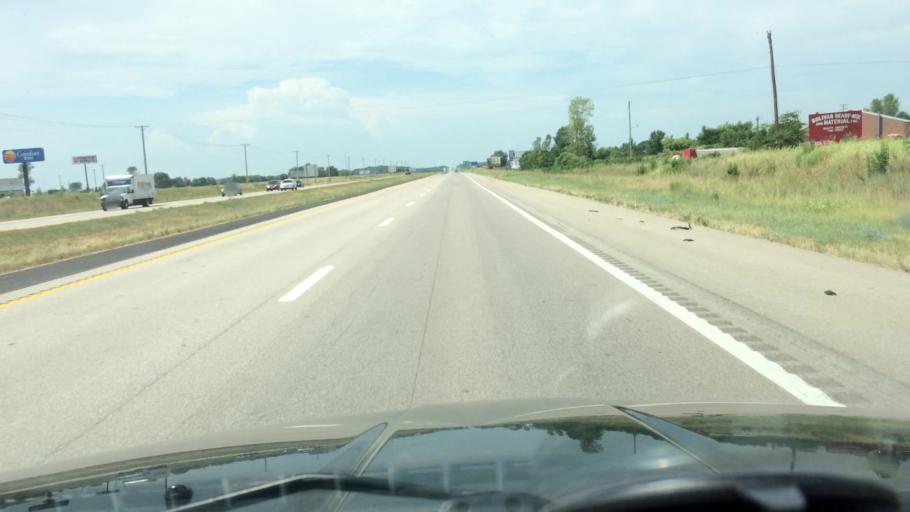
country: US
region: Missouri
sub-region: Polk County
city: Bolivar
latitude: 37.5981
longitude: -93.4363
